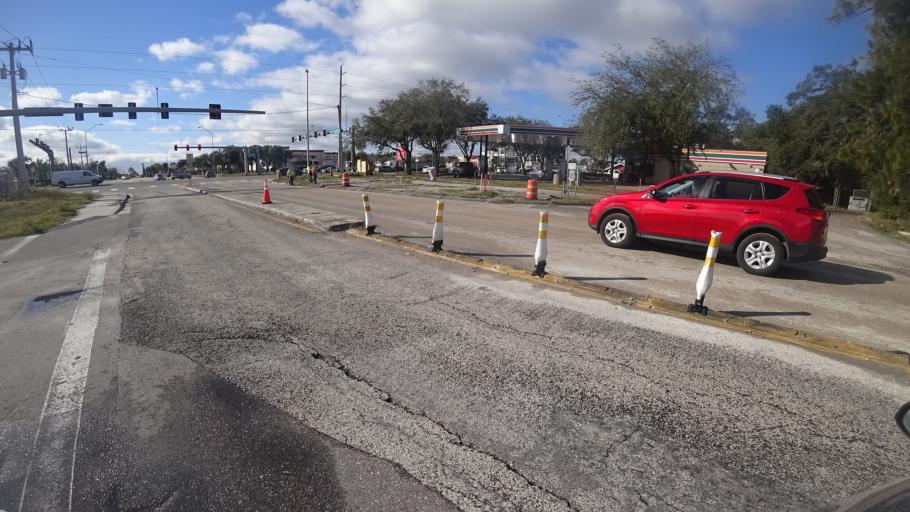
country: US
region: Florida
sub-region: Manatee County
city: Samoset
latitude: 27.4468
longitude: -82.5055
